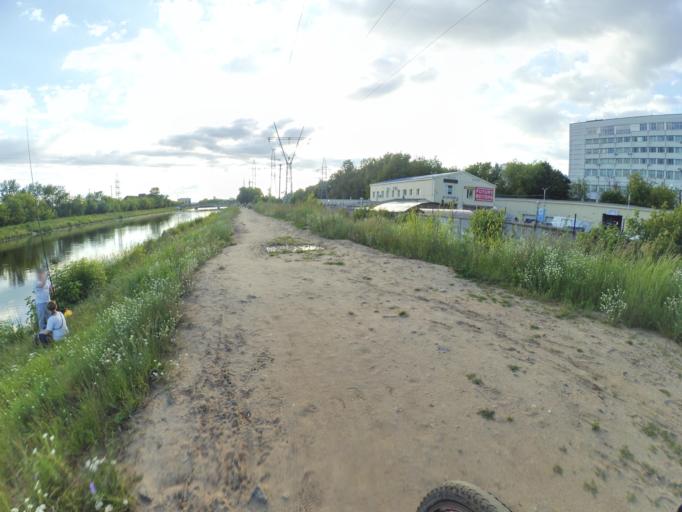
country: RU
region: Moscow
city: Pokrovskoye-Streshnevo
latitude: 55.8364
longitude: 37.4429
